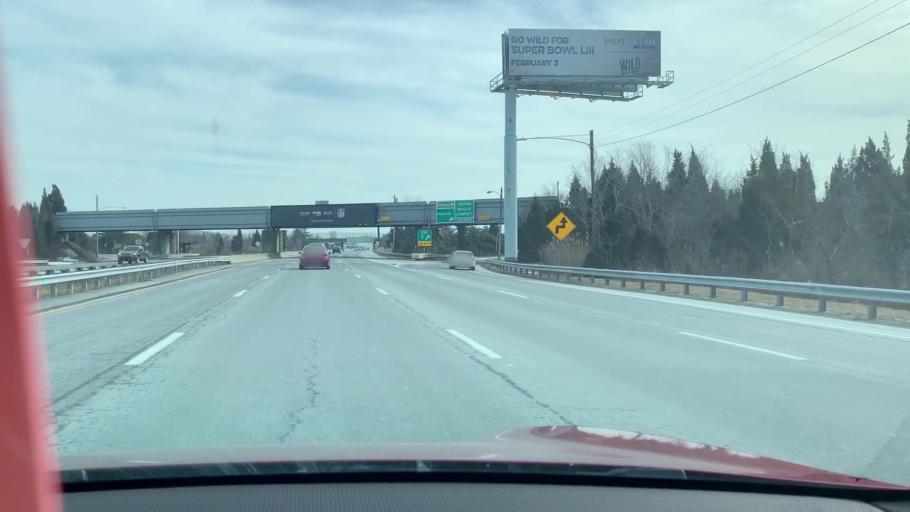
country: US
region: New Jersey
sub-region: Atlantic County
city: Ventnor City
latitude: 39.3777
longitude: -74.4832
